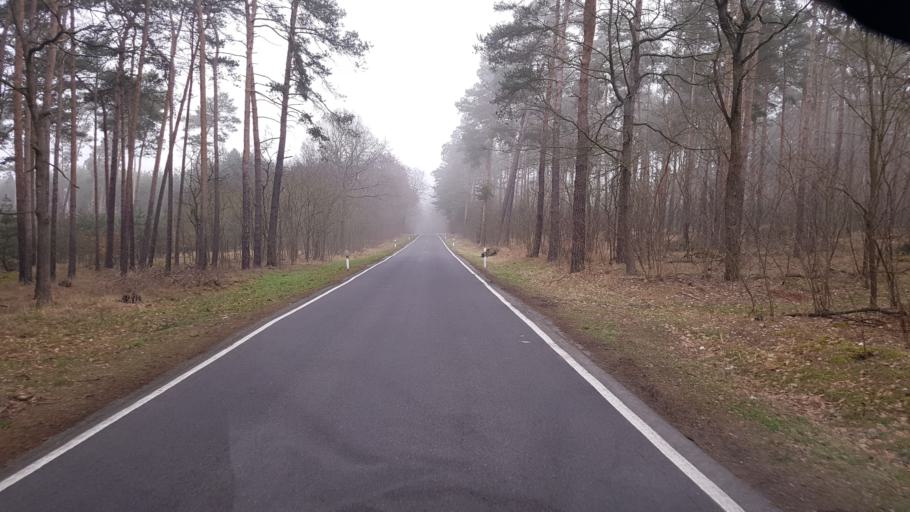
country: DE
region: Saxony-Anhalt
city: Holzdorf
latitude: 51.8226
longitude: 13.2157
